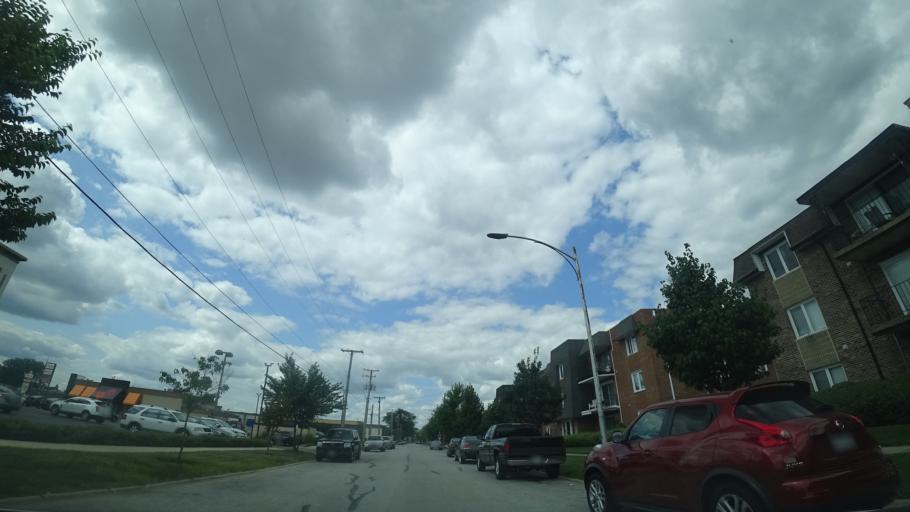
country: US
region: Illinois
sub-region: Cook County
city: Oak Lawn
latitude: 41.6956
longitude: -87.7387
